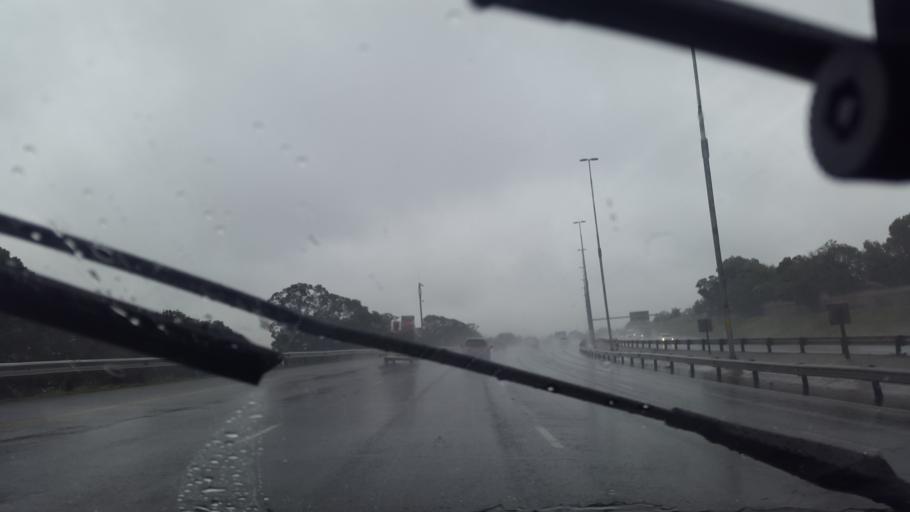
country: ZA
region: Gauteng
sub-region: City of Johannesburg Metropolitan Municipality
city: Johannesburg
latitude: -26.2650
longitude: 28.0194
